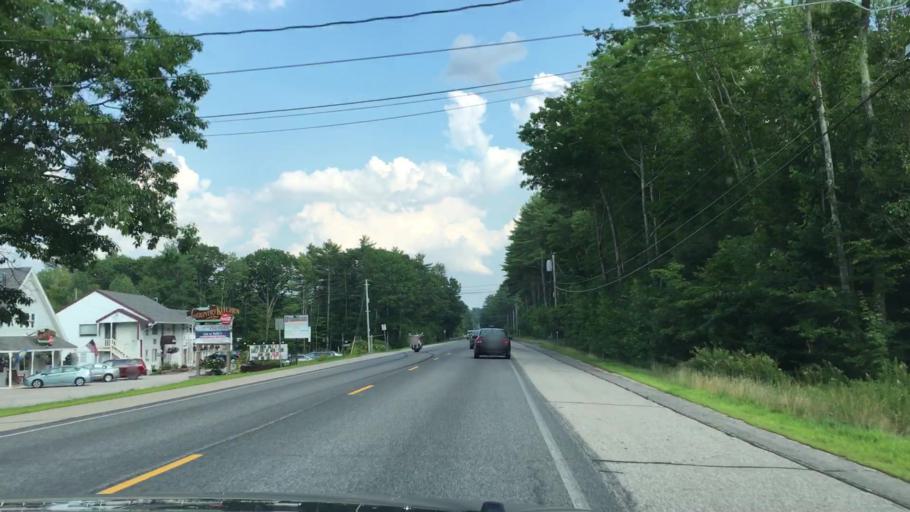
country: US
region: New Hampshire
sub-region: Strafford County
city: Farmington
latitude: 43.3929
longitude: -71.0941
